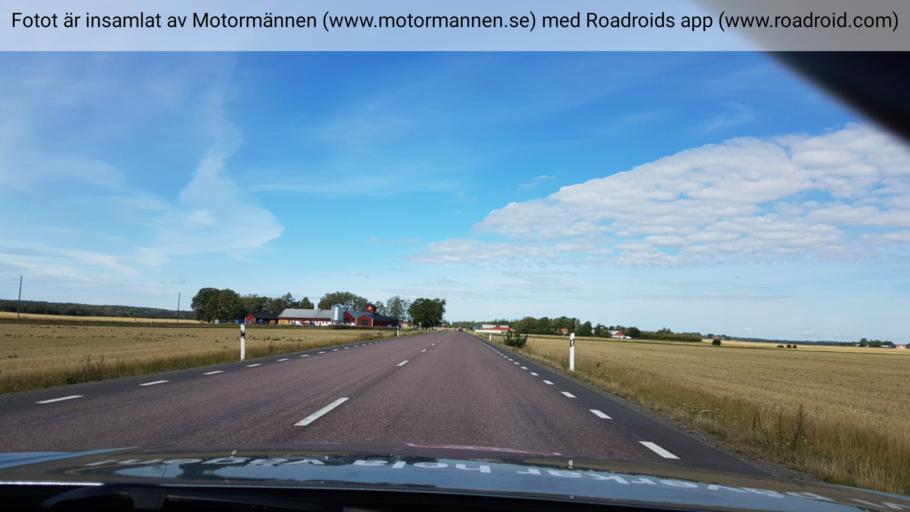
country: SE
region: Uppsala
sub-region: Uppsala Kommun
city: Gamla Uppsala
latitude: 59.9136
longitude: 17.5260
